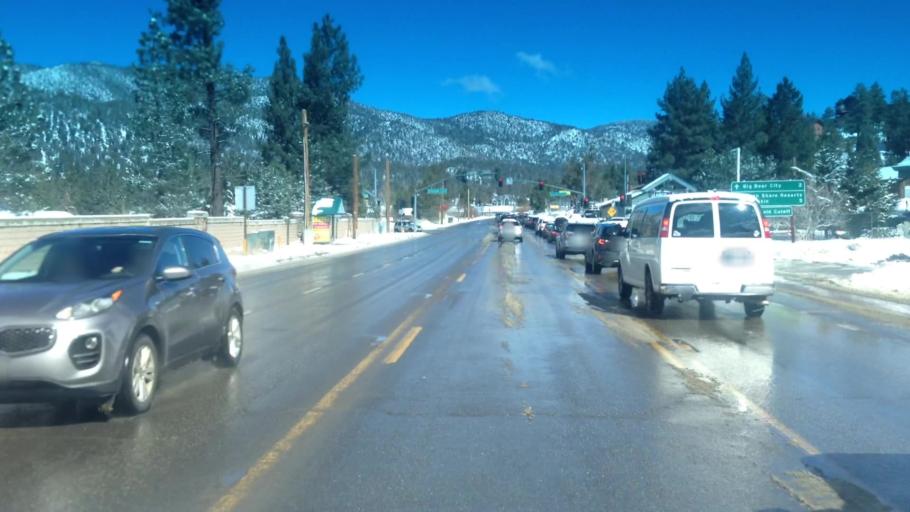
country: US
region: California
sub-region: San Bernardino County
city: Big Bear Lake
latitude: 34.2558
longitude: -116.8838
